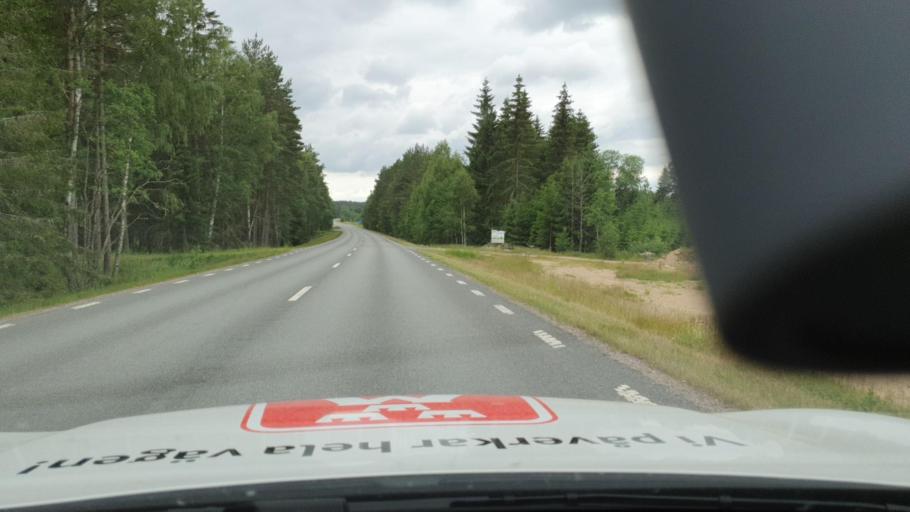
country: SE
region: Vaestra Goetaland
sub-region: Tidaholms Kommun
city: Olofstorp
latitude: 58.2236
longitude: 14.1149
